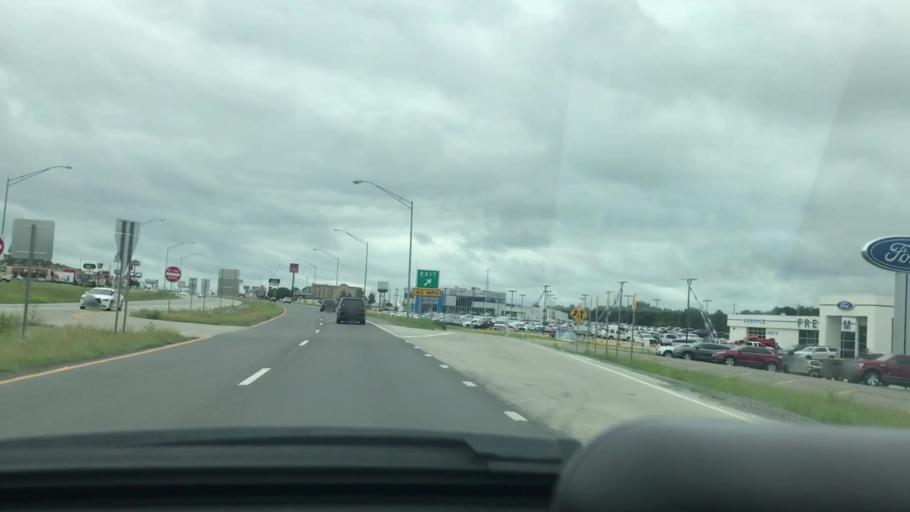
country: US
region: Oklahoma
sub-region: Pittsburg County
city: McAlester
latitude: 34.9089
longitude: -95.7455
